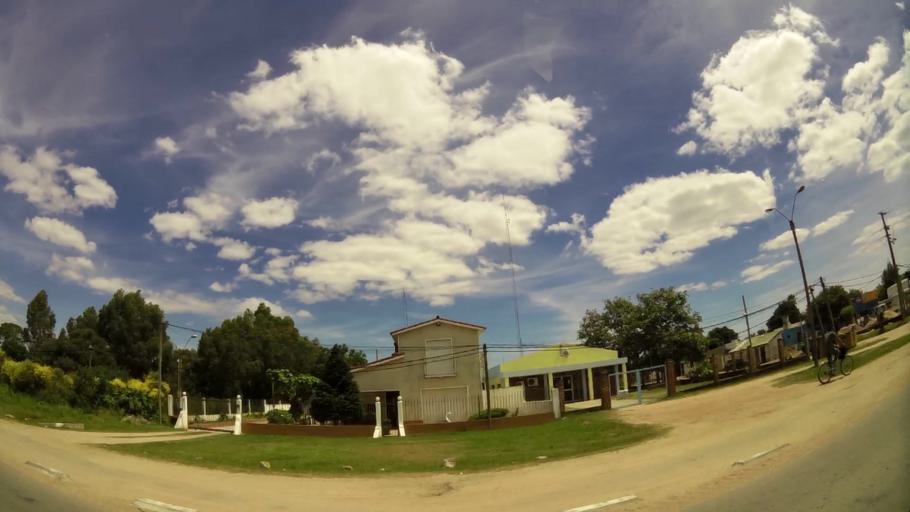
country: UY
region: San Jose
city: Delta del Tigre
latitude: -34.7387
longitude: -56.4403
